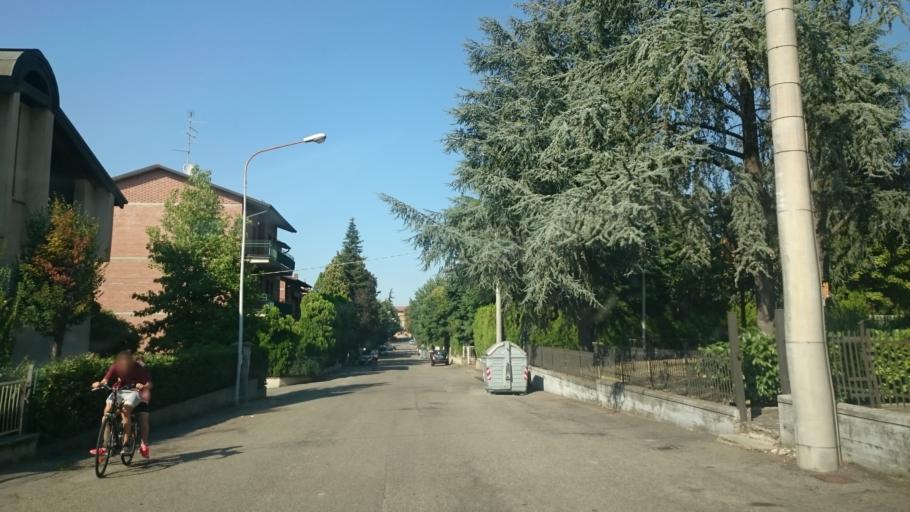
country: IT
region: Emilia-Romagna
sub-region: Provincia di Reggio Emilia
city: Ventoso
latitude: 44.5947
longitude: 10.6839
